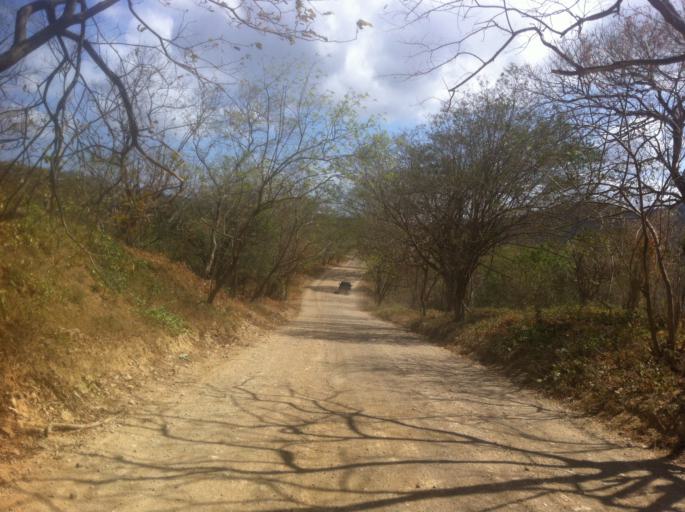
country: NI
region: Rivas
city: Tola
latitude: 11.4042
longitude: -86.0005
